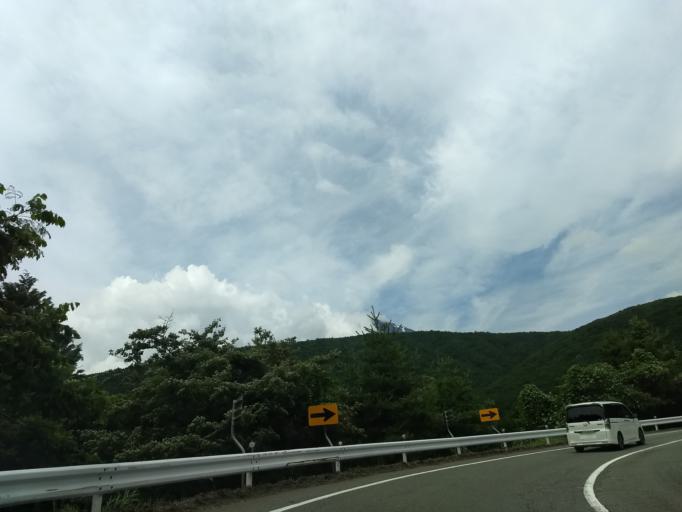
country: JP
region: Shizuoka
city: Gotemba
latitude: 35.3800
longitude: 138.8506
